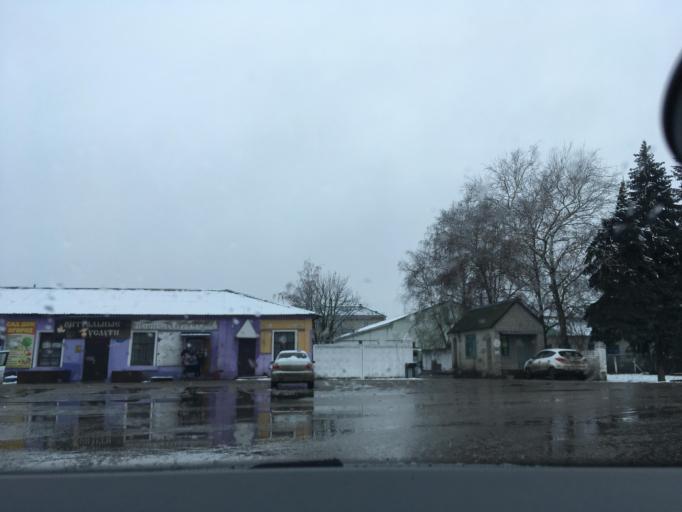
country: RU
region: Belgorod
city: Valuyki
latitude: 50.2019
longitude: 38.1215
